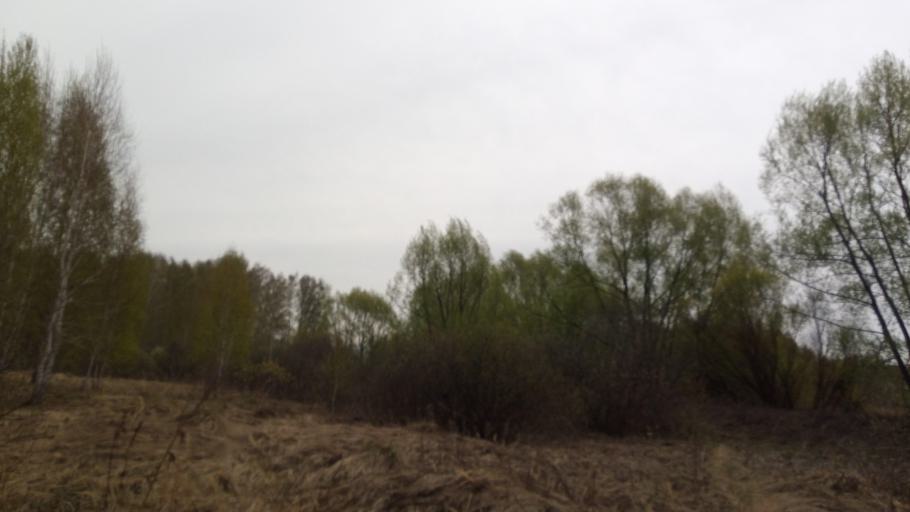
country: RU
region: Chelyabinsk
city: Timiryazevskiy
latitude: 55.0018
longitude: 60.8501
